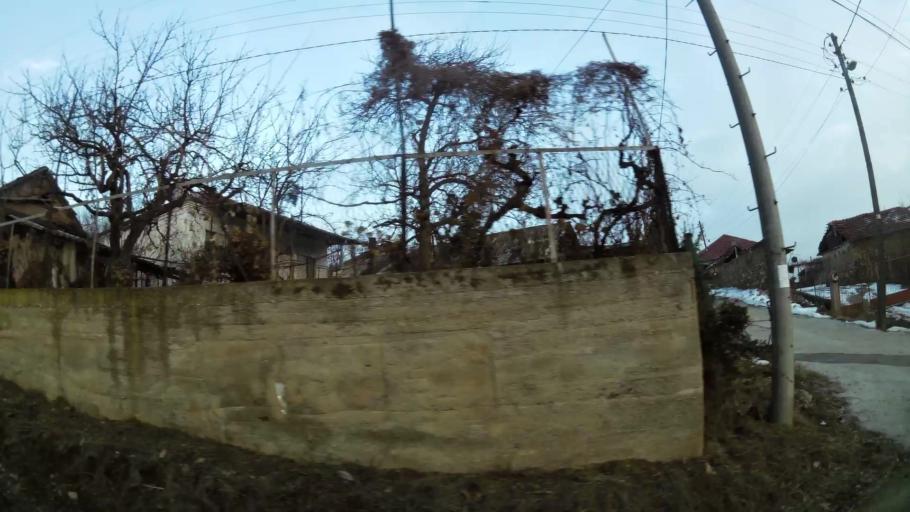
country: MK
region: Aracinovo
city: Arachinovo
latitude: 42.0330
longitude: 21.5484
